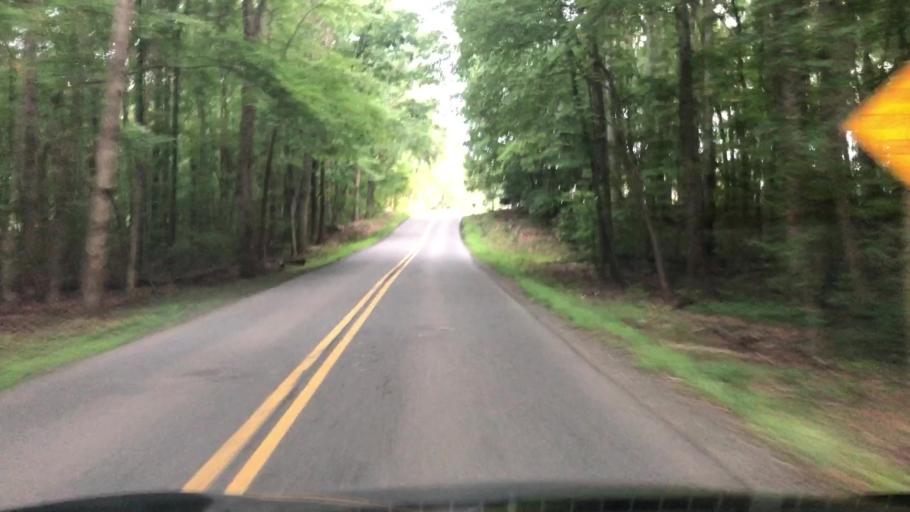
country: US
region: Virginia
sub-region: Fauquier County
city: Bealeton
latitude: 38.5291
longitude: -77.6707
